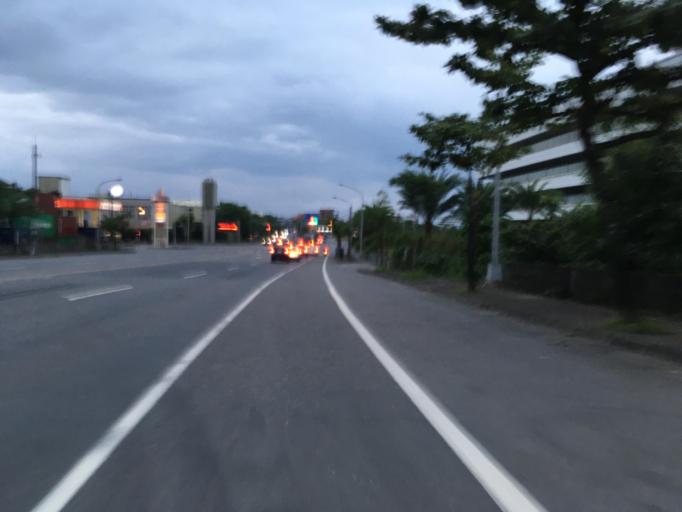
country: TW
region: Taiwan
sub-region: Yilan
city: Yilan
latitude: 24.6328
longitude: 121.8319
